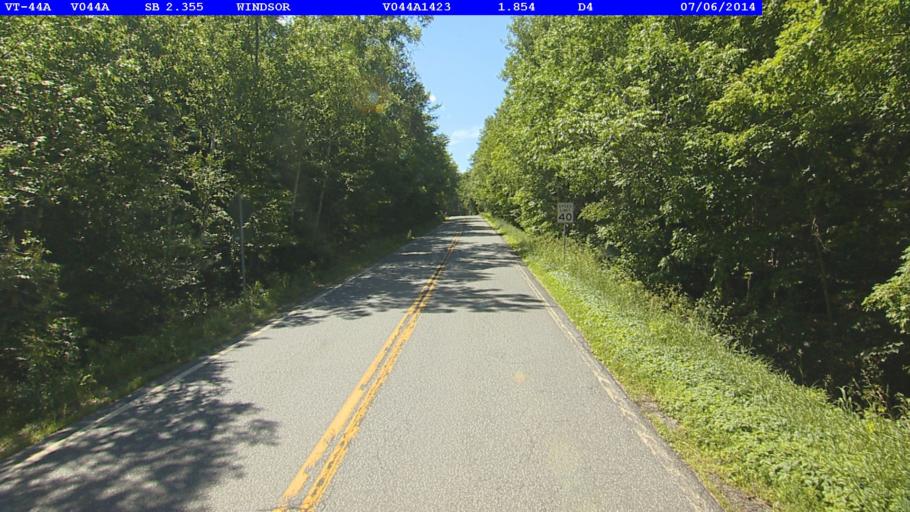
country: US
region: Vermont
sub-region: Windsor County
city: Windsor
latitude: 43.4518
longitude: -72.4172
